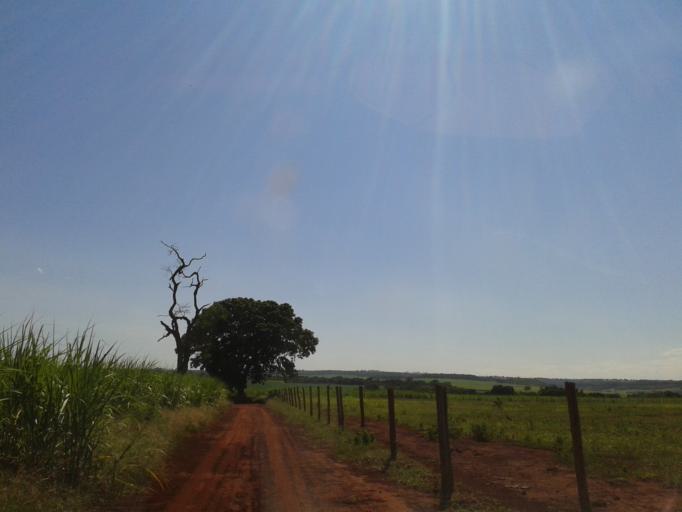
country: BR
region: Minas Gerais
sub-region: Centralina
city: Centralina
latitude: -18.6301
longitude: -49.2539
